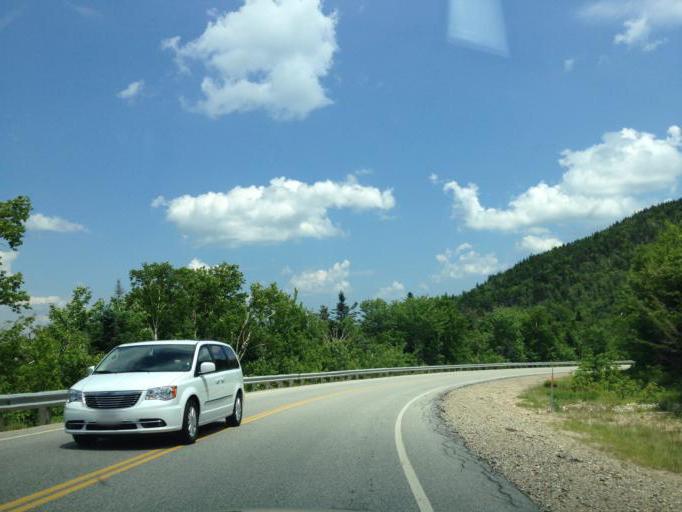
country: US
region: New Hampshire
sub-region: Grafton County
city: Woodstock
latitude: 44.0223
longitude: -71.4821
